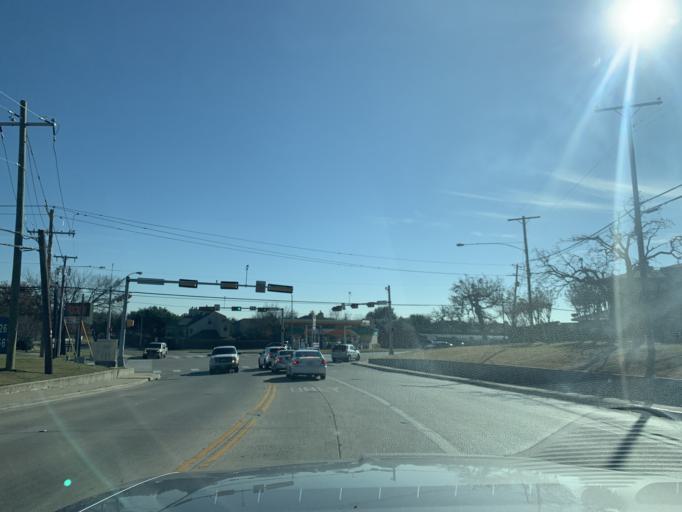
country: US
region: Texas
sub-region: Tarrant County
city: Bedford
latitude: 32.8448
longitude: -97.1434
